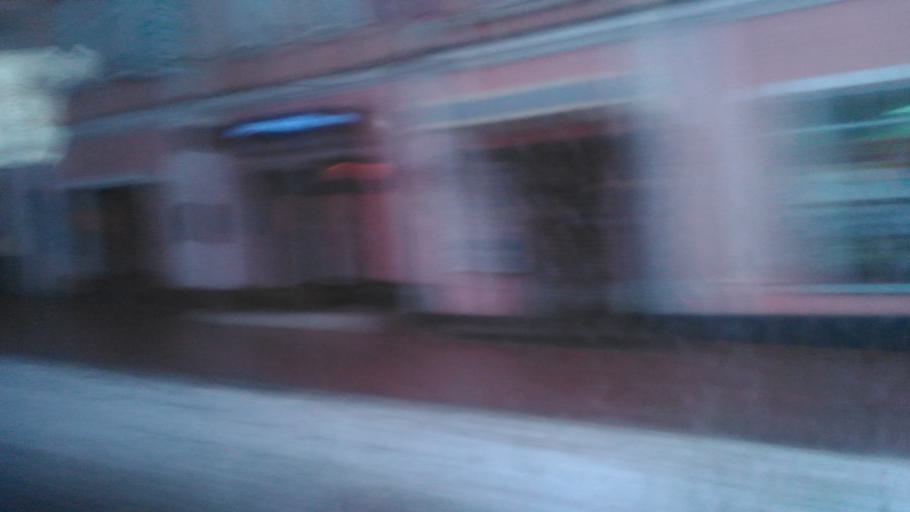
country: RU
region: Tula
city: Tula
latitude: 54.1887
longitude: 37.6125
